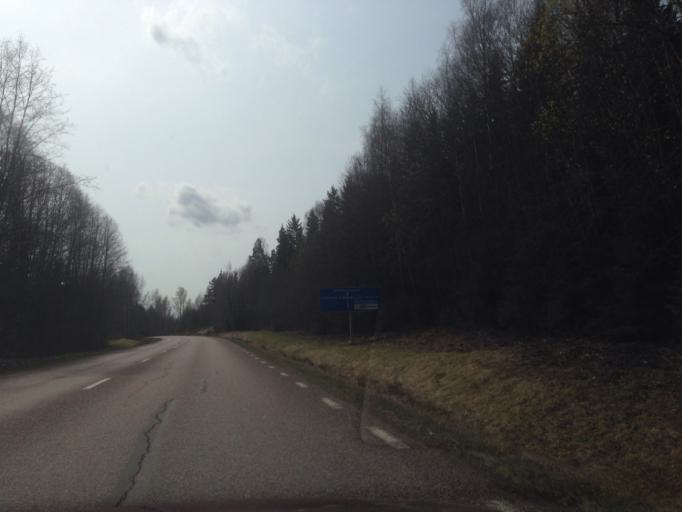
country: SE
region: Dalarna
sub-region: Ludvika Kommun
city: Grangesberg
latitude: 60.2145
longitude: 14.9571
